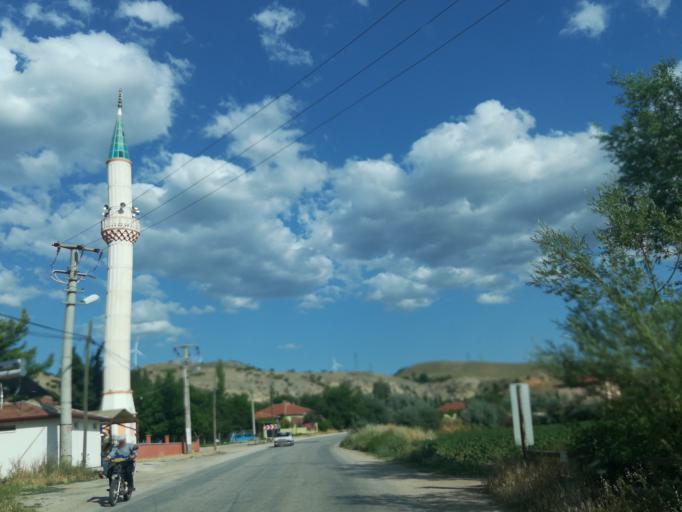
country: TR
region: Afyonkarahisar
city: Dinar
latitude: 38.0826
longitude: 30.1662
